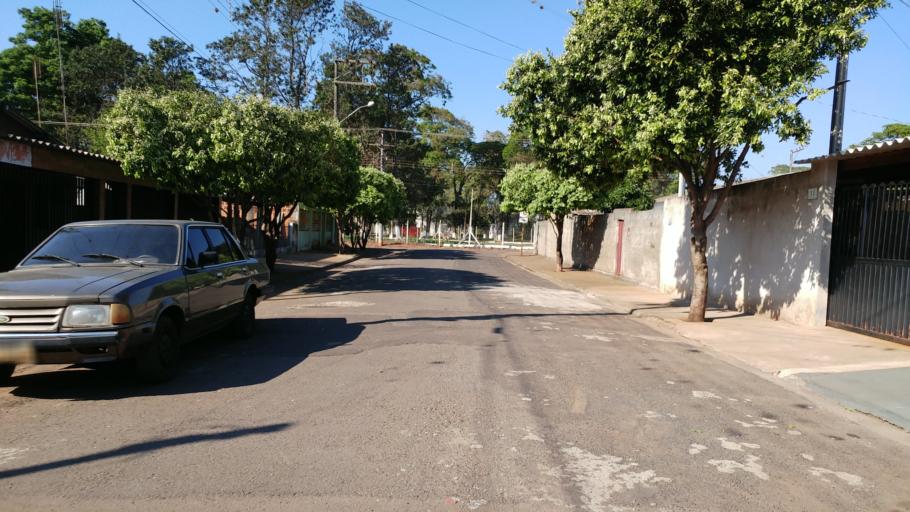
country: BR
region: Sao Paulo
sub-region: Paraguacu Paulista
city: Paraguacu Paulista
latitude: -22.4203
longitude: -50.5708
